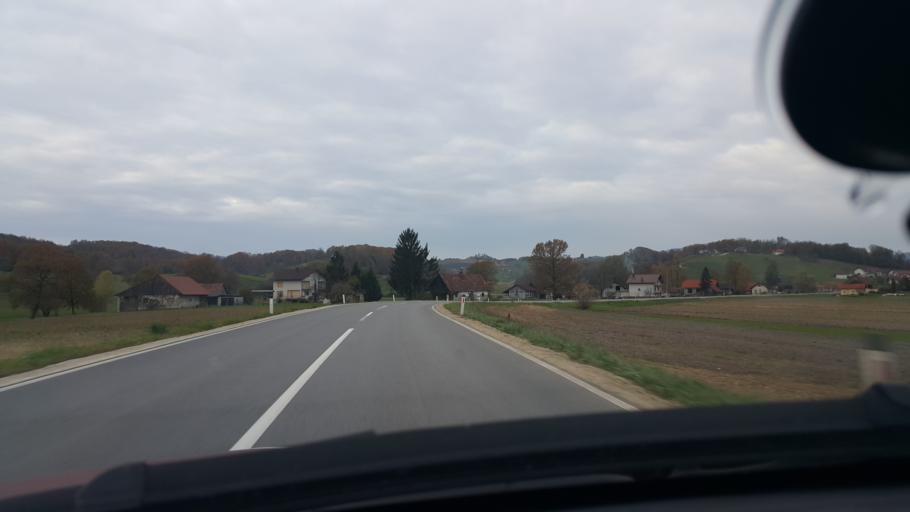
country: SI
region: Podcetrtek
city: Podcetrtek
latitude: 46.1058
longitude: 15.6063
